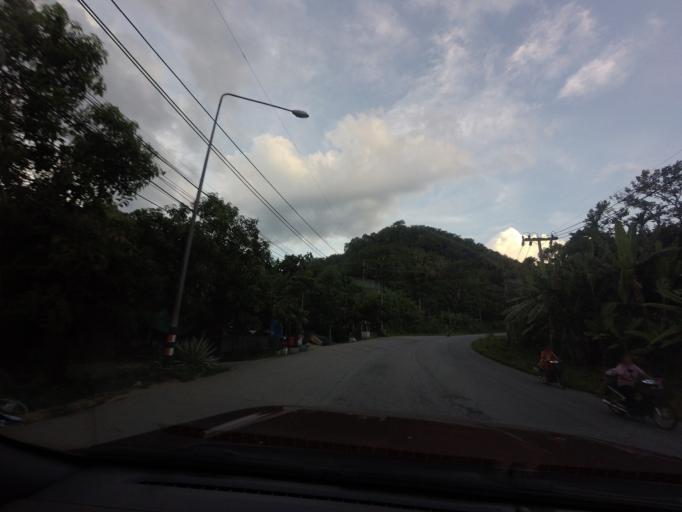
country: TH
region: Yala
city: Than To
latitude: 6.0682
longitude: 101.1984
